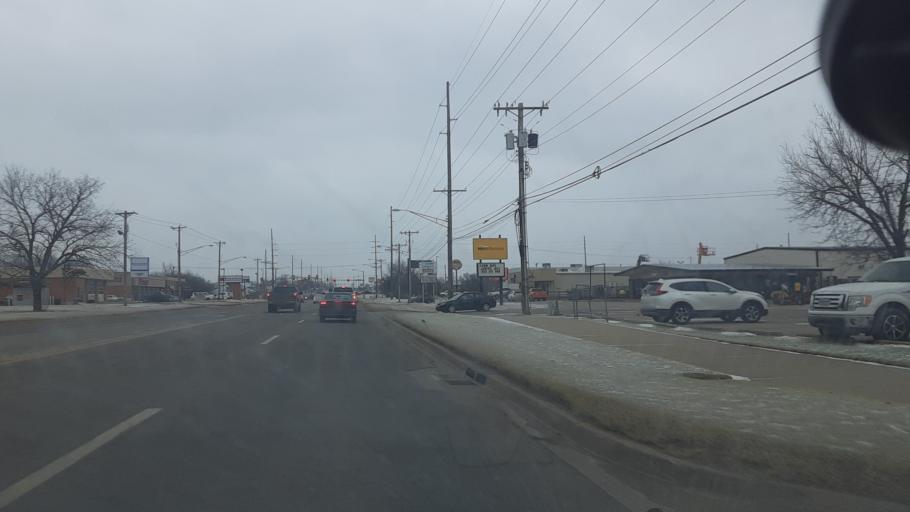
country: US
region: Oklahoma
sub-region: Payne County
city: Stillwater
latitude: 36.1211
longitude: -97.0514
